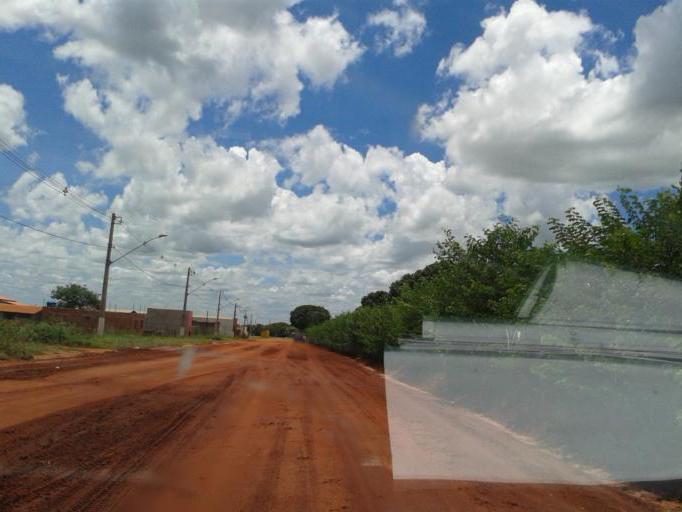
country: BR
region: Minas Gerais
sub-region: Santa Vitoria
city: Santa Vitoria
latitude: -18.8563
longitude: -50.1321
